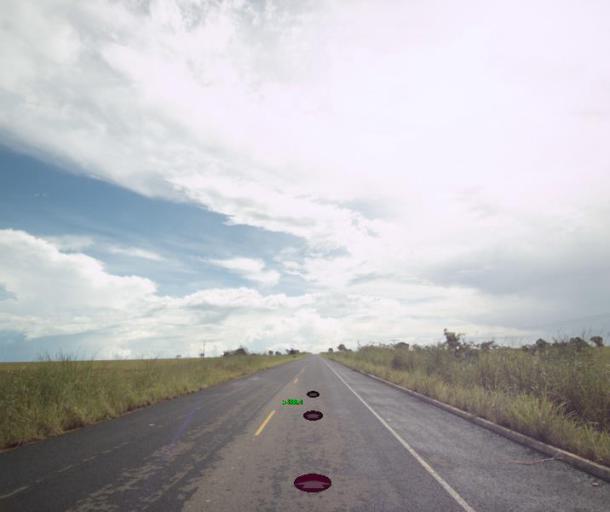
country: BR
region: Goias
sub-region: Sao Miguel Do Araguaia
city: Sao Miguel do Araguaia
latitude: -13.2984
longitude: -50.2488
